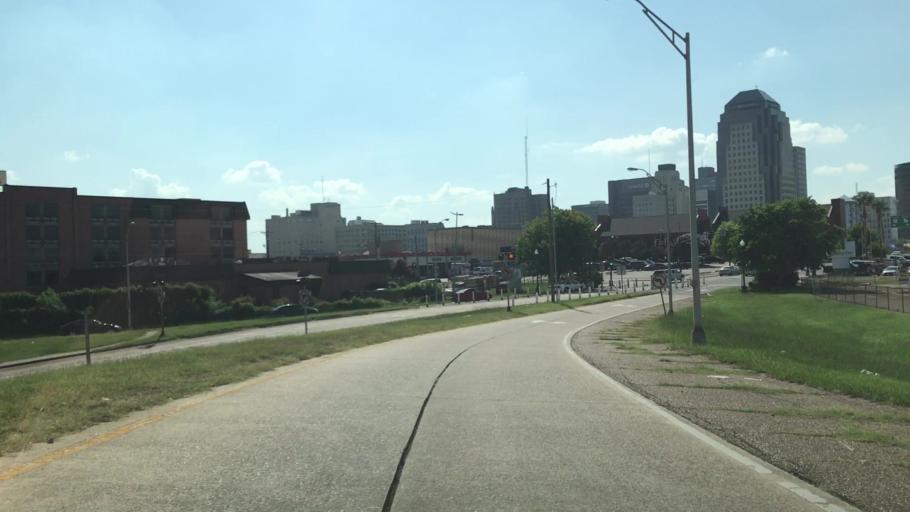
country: US
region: Louisiana
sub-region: Bossier Parish
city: Bossier City
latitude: 32.5113
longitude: -93.7423
